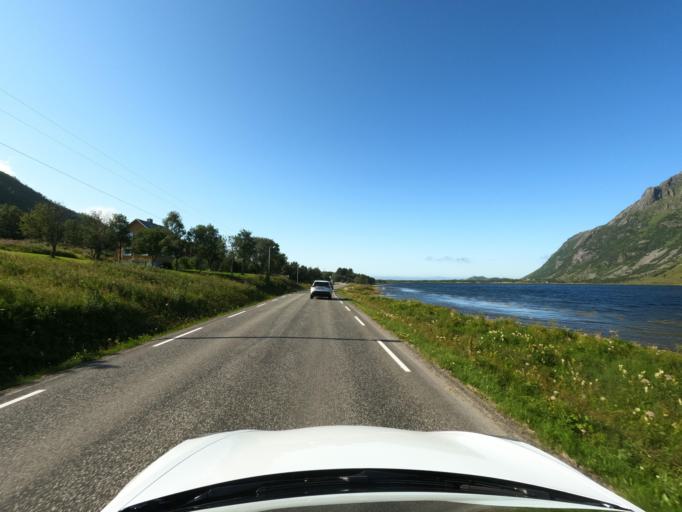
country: NO
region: Nordland
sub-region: Vestvagoy
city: Evjen
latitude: 68.2793
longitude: 13.9210
